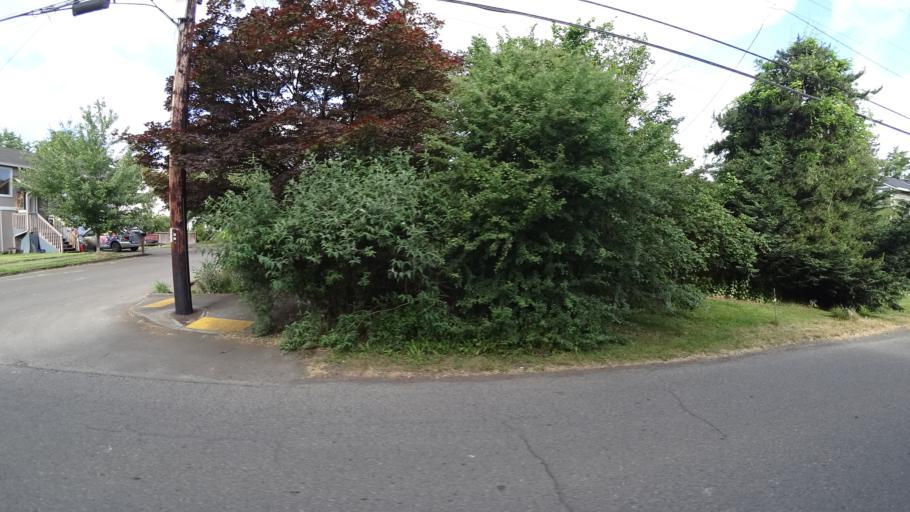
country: US
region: Oregon
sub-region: Multnomah County
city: Lents
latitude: 45.4791
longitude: -122.5574
